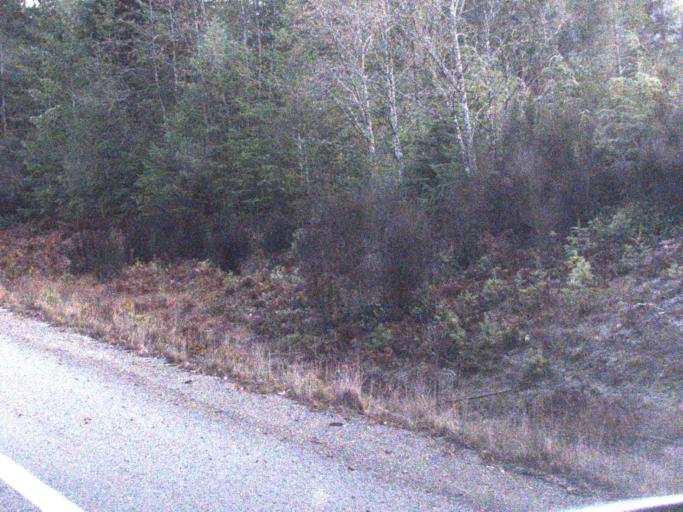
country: US
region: Washington
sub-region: Snohomish County
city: Darrington
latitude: 48.2606
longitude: -121.6210
